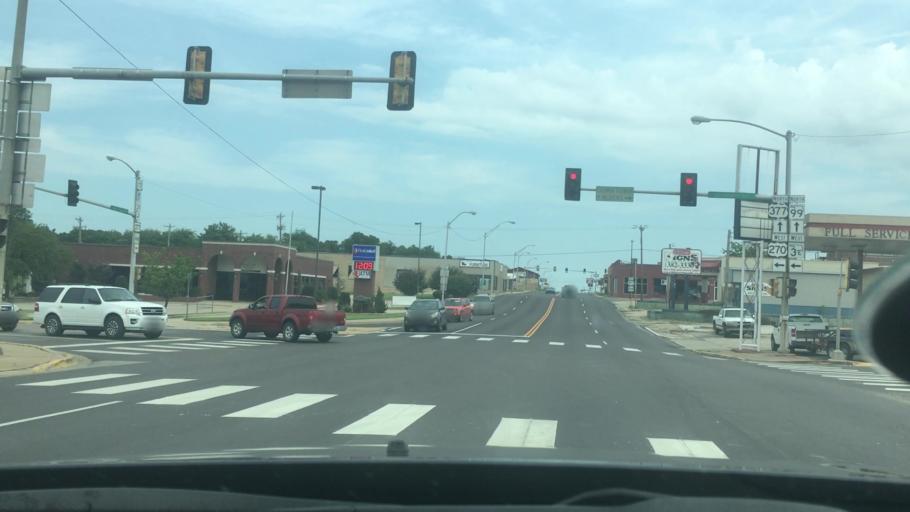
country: US
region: Oklahoma
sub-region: Seminole County
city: Seminole
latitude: 35.2242
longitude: -96.6710
